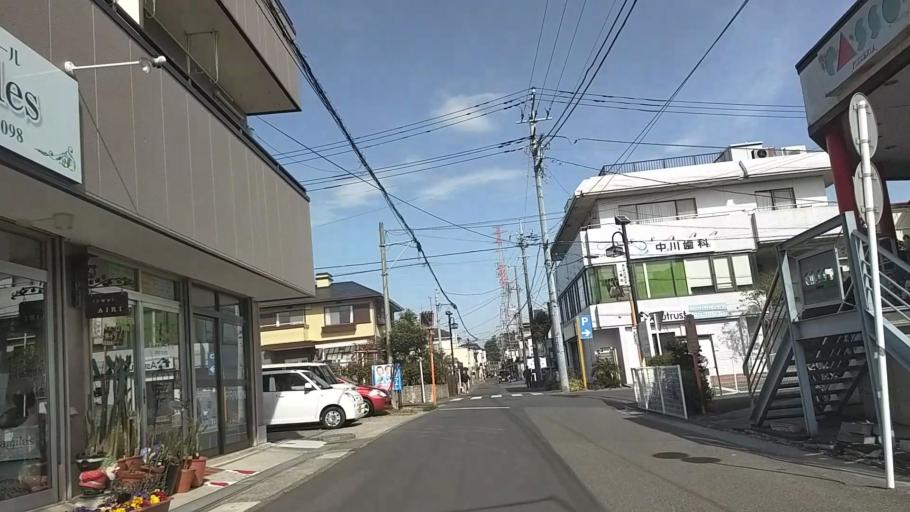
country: JP
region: Kanagawa
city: Chigasaki
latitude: 35.3706
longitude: 139.3882
